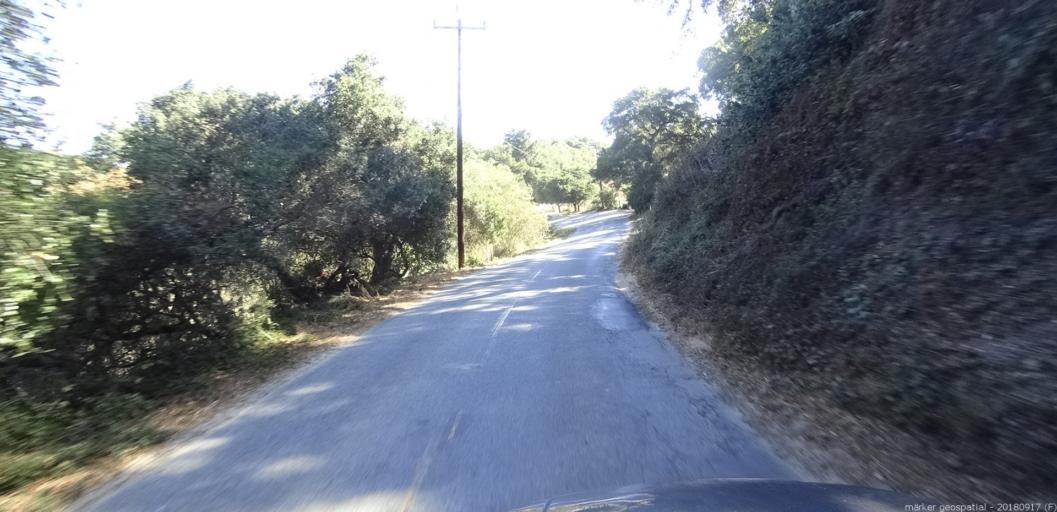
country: US
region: California
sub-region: Monterey County
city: Elkhorn
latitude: 36.8204
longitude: -121.7287
